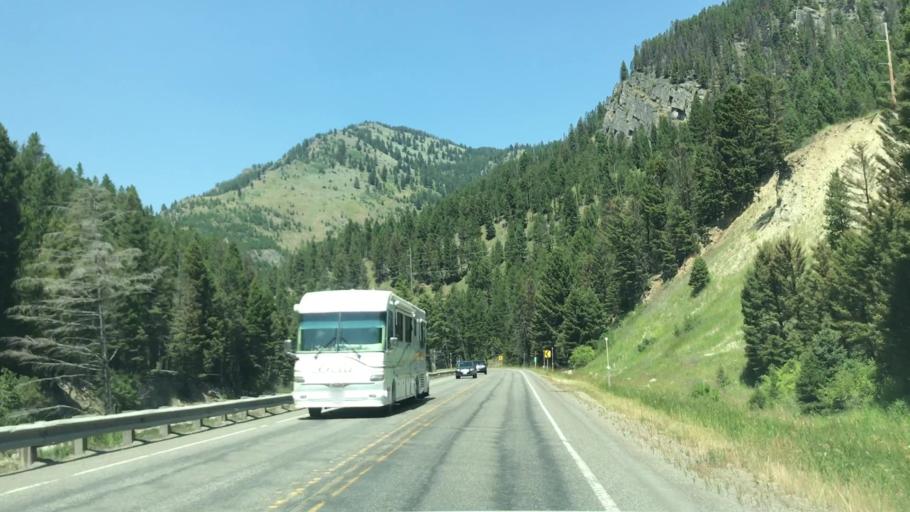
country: US
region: Montana
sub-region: Gallatin County
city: Big Sky
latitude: 45.3836
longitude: -111.1937
